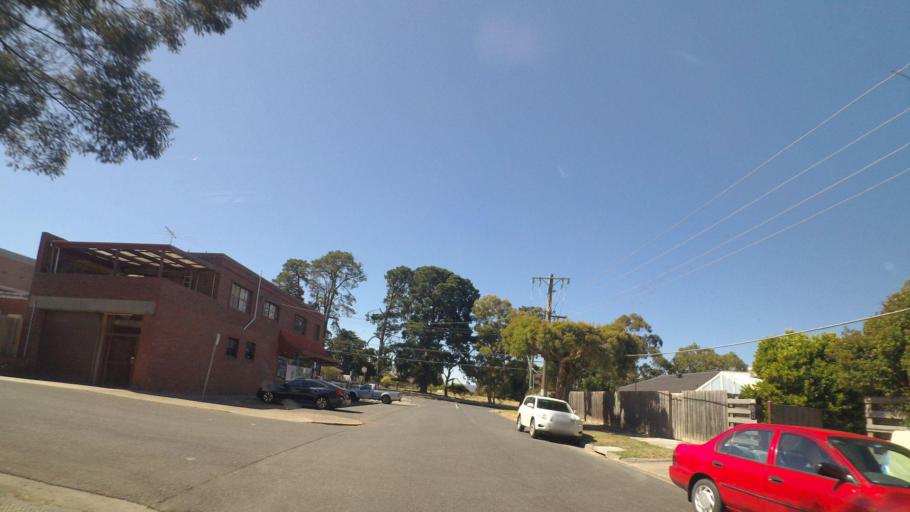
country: AU
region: Victoria
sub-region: Yarra Ranges
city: Chirnside Park
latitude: -37.7450
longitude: 145.3259
